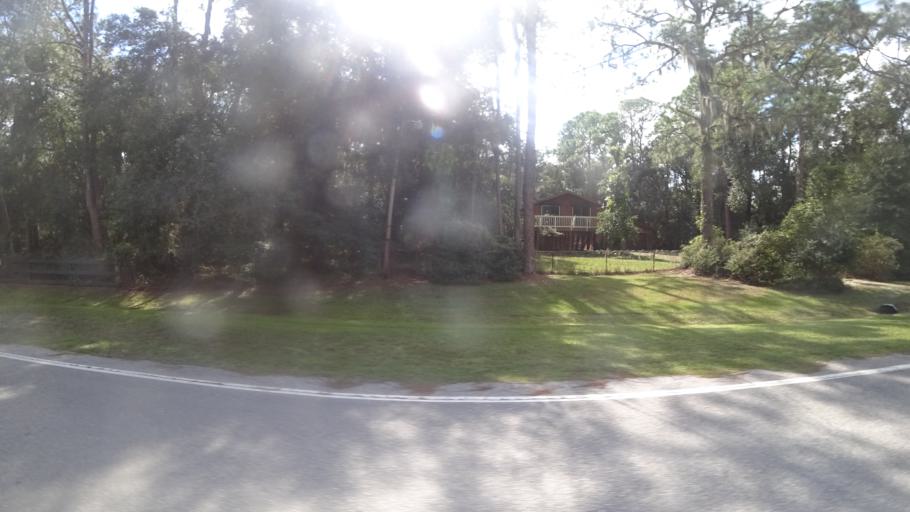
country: US
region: Florida
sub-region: Hillsborough County
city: Sun City Center
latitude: 27.6563
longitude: -82.3785
